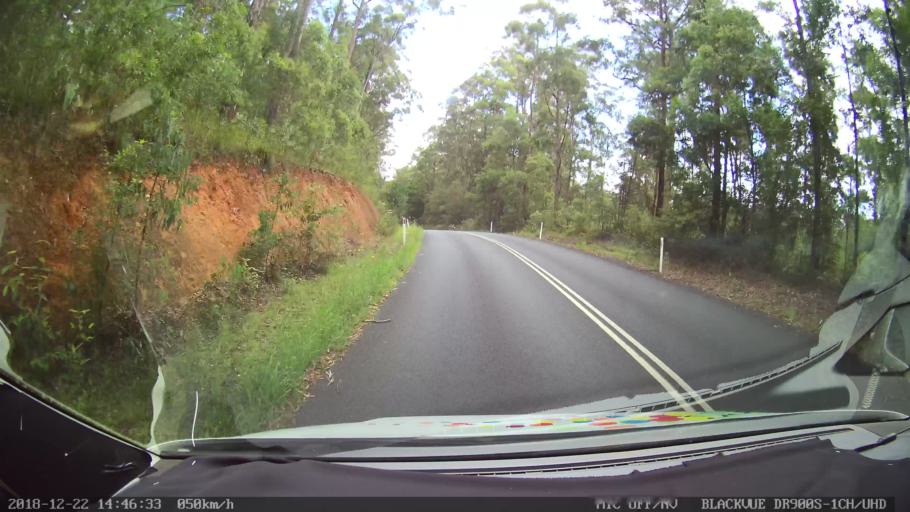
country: AU
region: New South Wales
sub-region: Bellingen
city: Dorrigo
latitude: -30.1729
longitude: 152.5609
